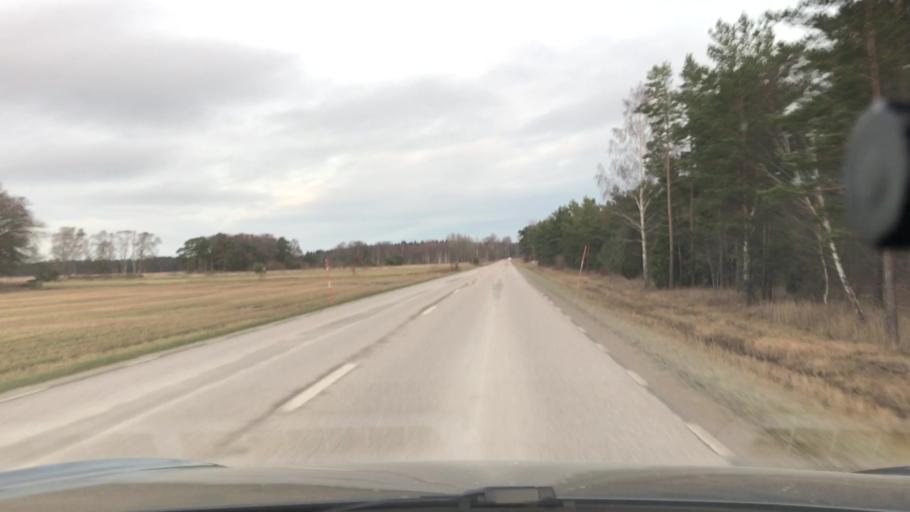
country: SE
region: Gotland
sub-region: Gotland
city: Slite
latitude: 57.7181
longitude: 18.5549
